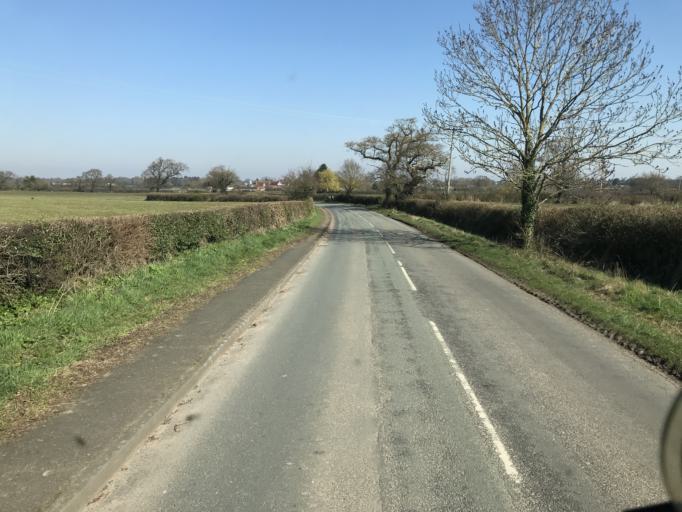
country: GB
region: England
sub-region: Cheshire West and Chester
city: Waverton
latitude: 53.1566
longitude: -2.8295
